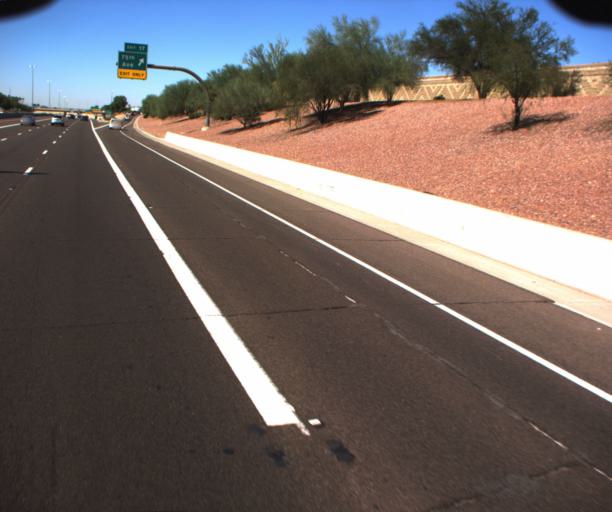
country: US
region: Arizona
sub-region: Maricopa County
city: Peoria
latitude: 33.6678
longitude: -112.2134
